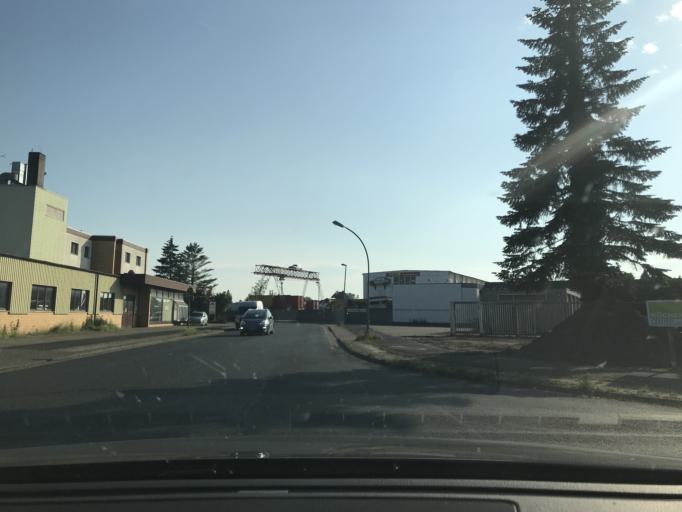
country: DE
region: Lower Saxony
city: Lehrte
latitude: 52.3864
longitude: 9.9677
